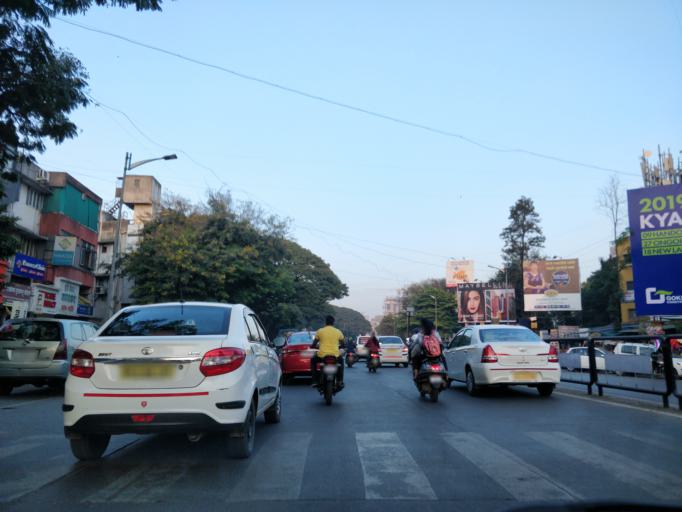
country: IN
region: Maharashtra
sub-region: Pune Division
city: Pune
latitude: 18.5034
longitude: 73.8198
